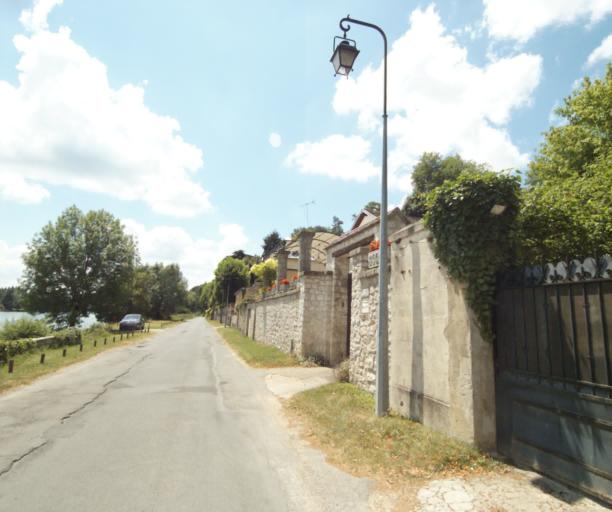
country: FR
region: Ile-de-France
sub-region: Departement de Seine-et-Marne
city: Samois-sur-Seine
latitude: 48.4460
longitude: 2.7513
